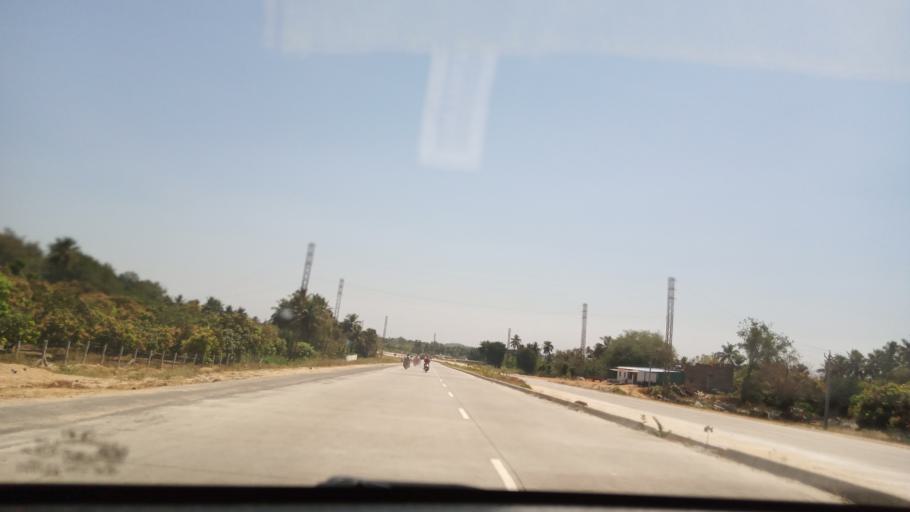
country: IN
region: Andhra Pradesh
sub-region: Chittoor
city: Chittoor
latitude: 13.1967
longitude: 78.9851
